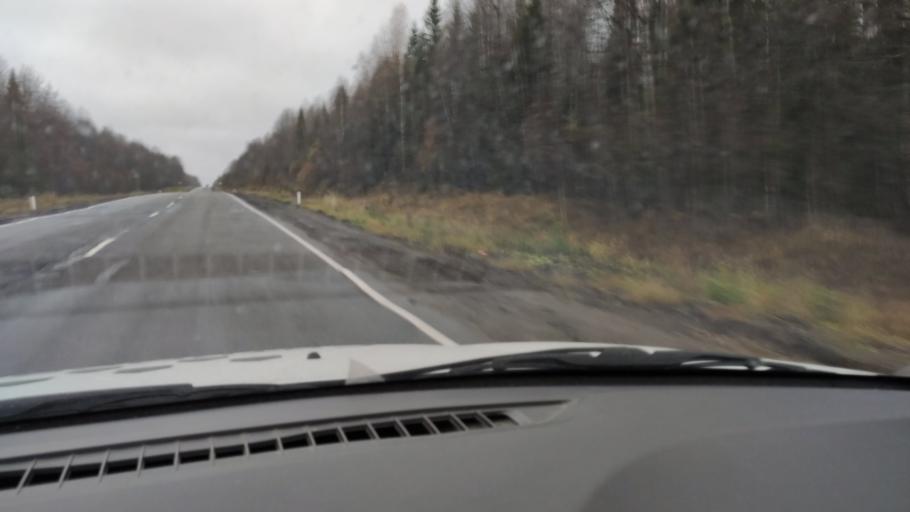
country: RU
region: Kirov
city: Omutninsk
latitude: 58.7566
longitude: 52.0326
